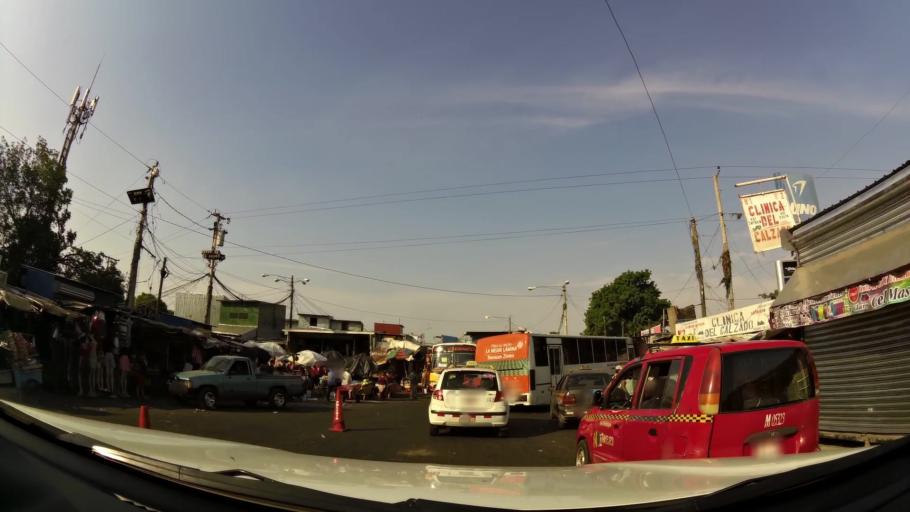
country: NI
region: Managua
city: Managua
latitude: 12.1452
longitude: -86.2607
